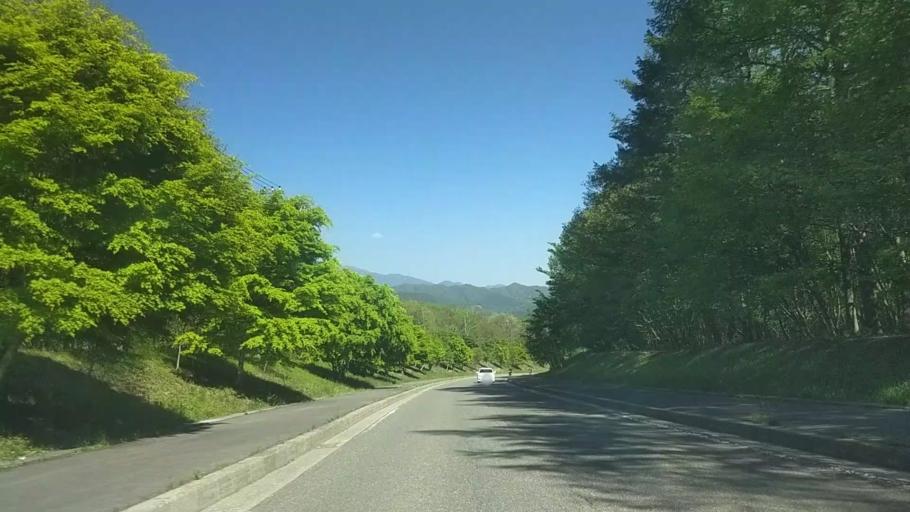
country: JP
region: Yamanashi
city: Nirasaki
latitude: 35.9212
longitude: 138.4307
